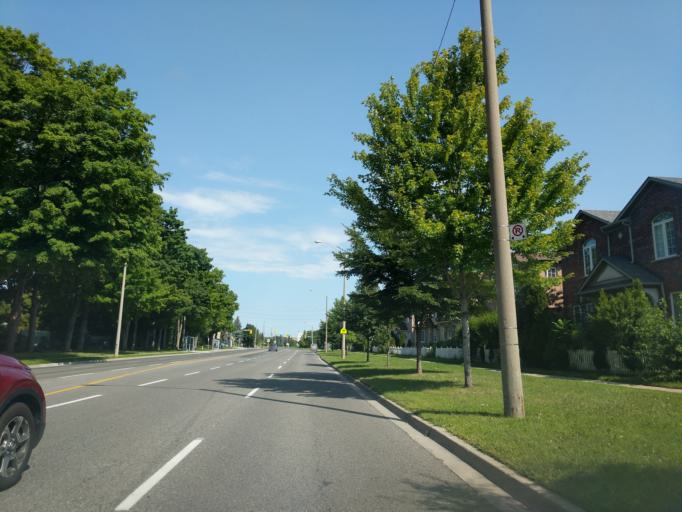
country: CA
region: Ontario
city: Scarborough
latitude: 43.8147
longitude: -79.2268
